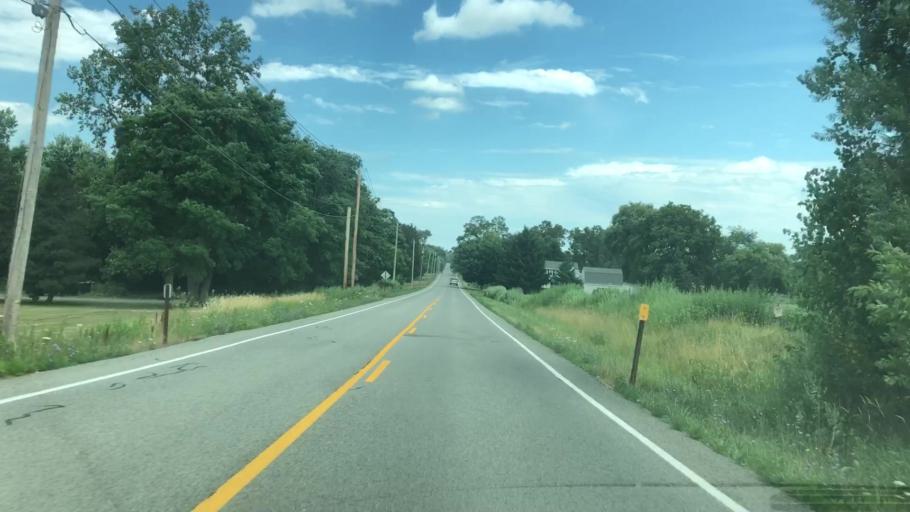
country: US
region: New York
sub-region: Wayne County
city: Macedon
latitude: 43.1066
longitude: -77.3523
